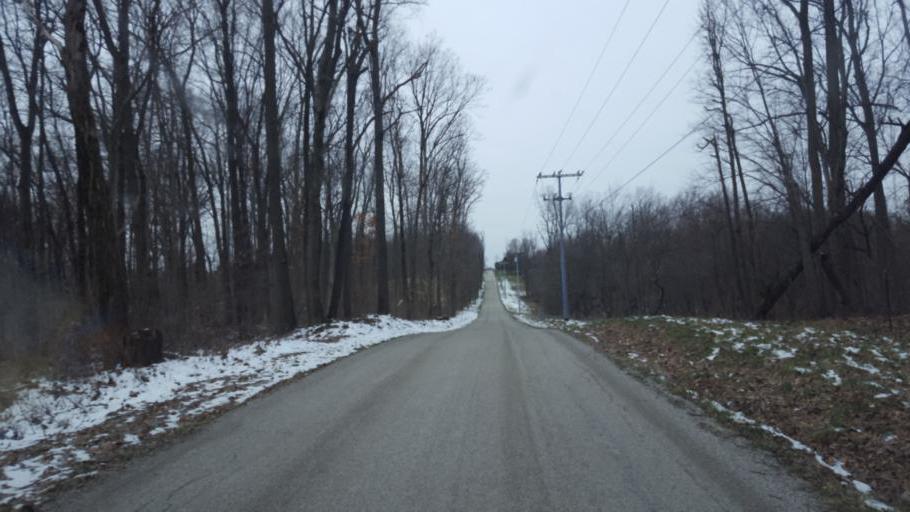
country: US
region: Ohio
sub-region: Sandusky County
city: Bellville
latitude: 40.5800
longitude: -82.4672
